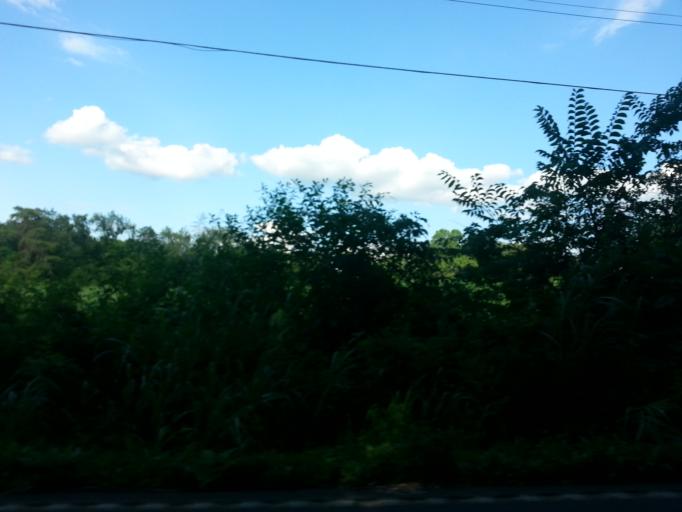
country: US
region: Tennessee
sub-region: Loudon County
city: Greenback
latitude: 35.6361
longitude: -84.0998
